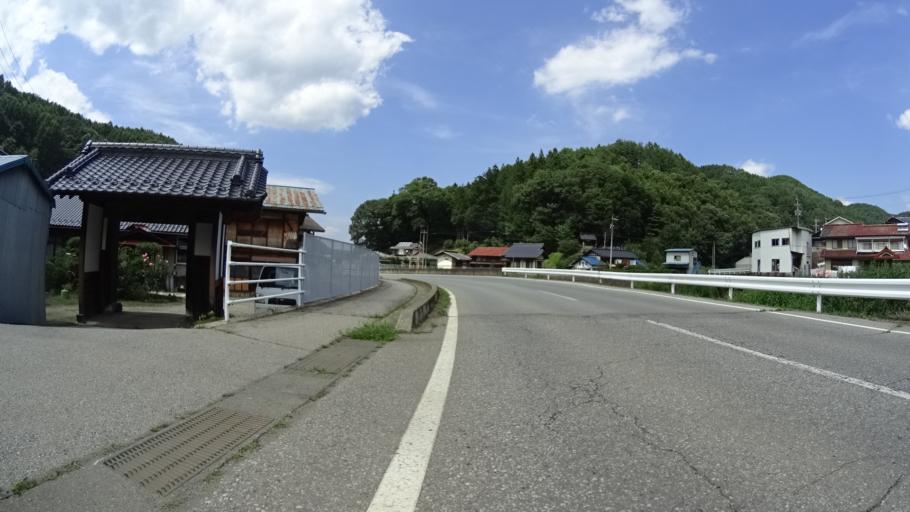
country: JP
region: Nagano
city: Saku
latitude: 36.0684
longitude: 138.4988
